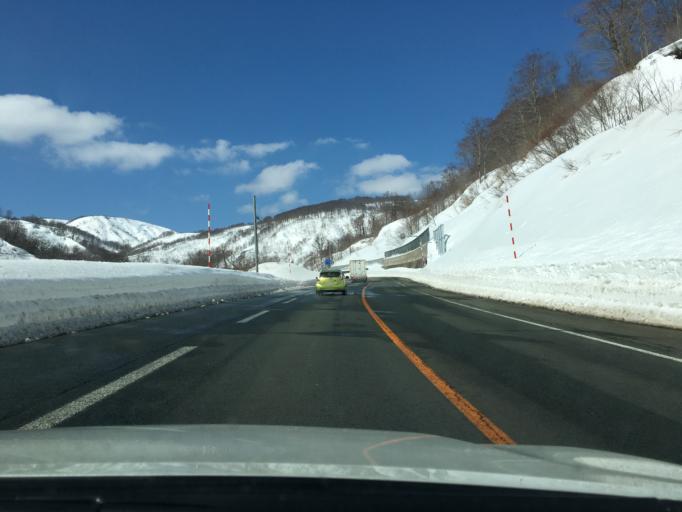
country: JP
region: Yamagata
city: Tsuruoka
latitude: 38.4968
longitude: 139.9699
